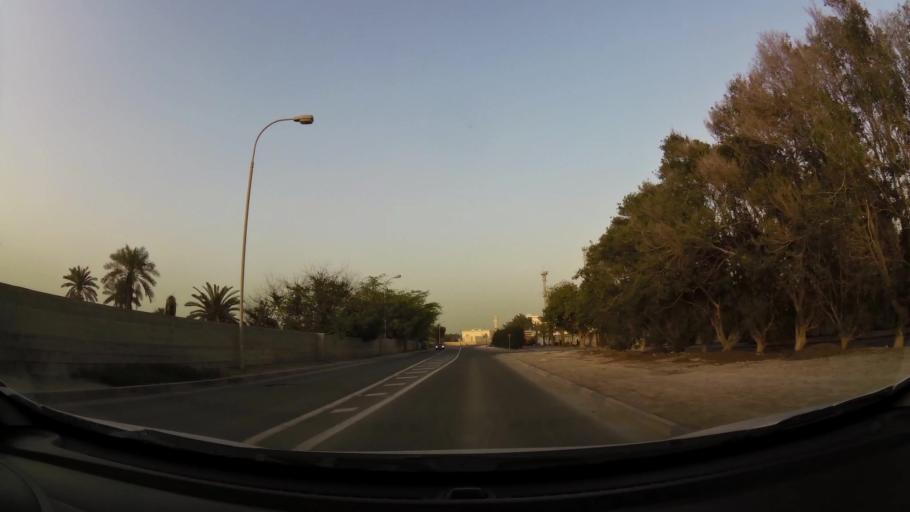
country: BH
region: Northern
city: Madinat `Isa
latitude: 26.1958
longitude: 50.4709
